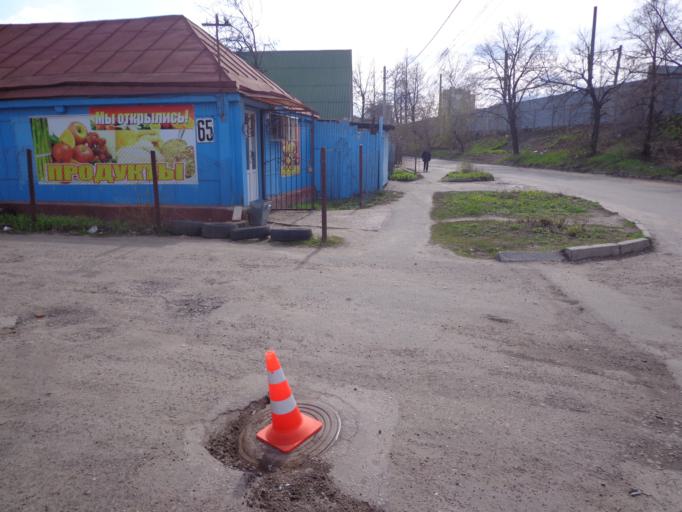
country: RU
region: Voronezj
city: Voronezh
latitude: 51.6930
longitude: 39.2272
